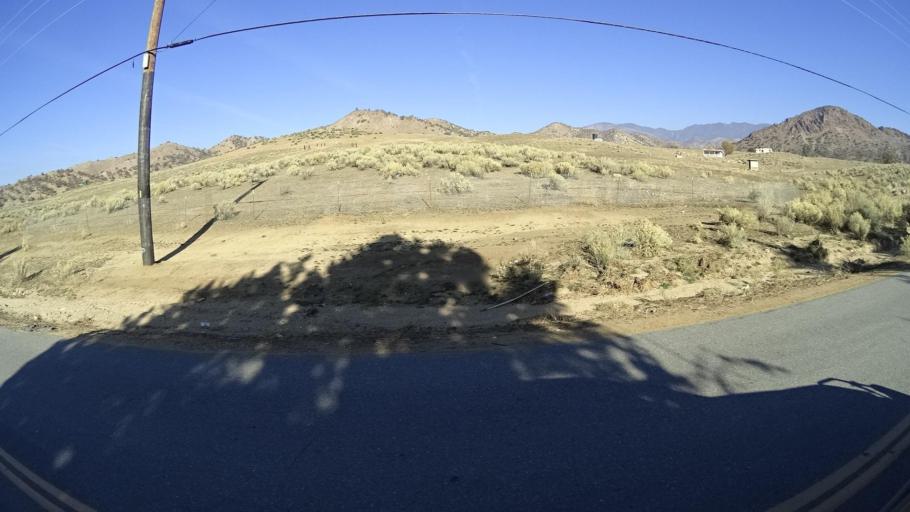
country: US
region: California
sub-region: Kern County
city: Tehachapi
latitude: 35.3177
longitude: -118.3939
